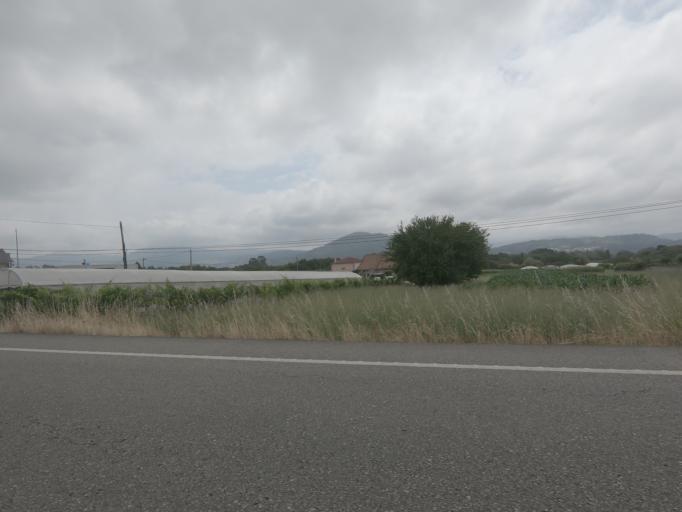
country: ES
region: Galicia
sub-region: Provincia de Pontevedra
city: O Rosal
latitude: 41.9231
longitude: -8.8092
